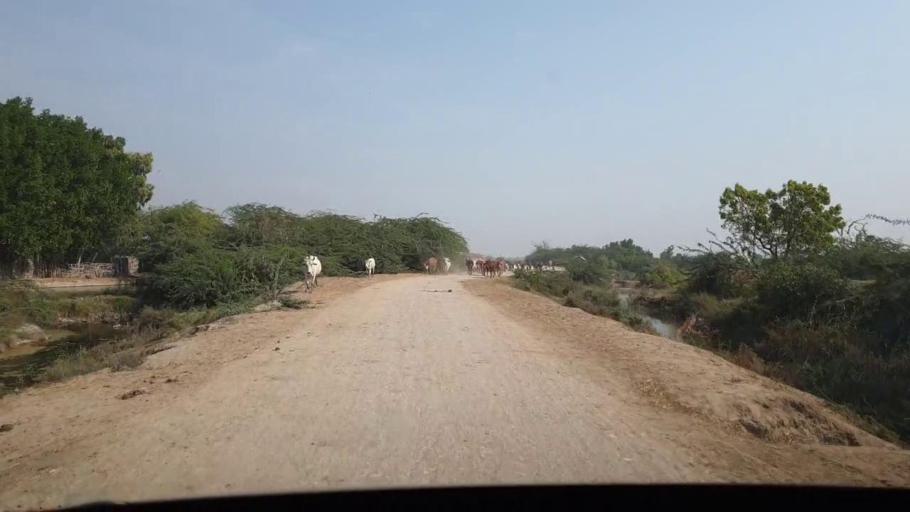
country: PK
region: Sindh
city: Chuhar Jamali
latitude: 24.2656
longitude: 67.9433
